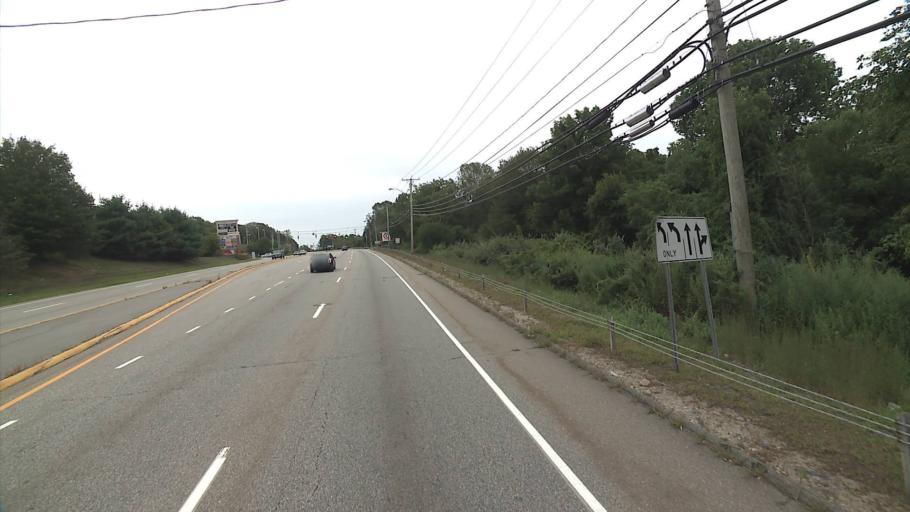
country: US
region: Connecticut
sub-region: New London County
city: Central Waterford
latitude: 41.3796
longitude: -72.1508
